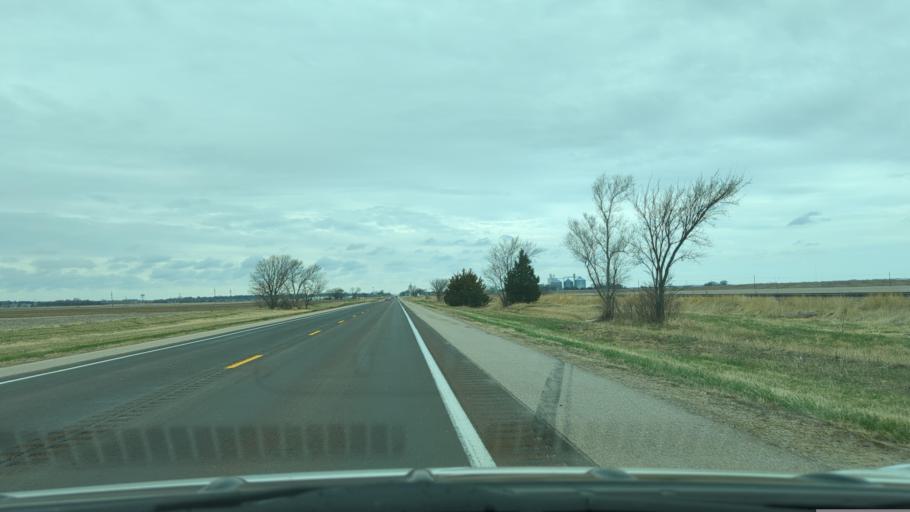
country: US
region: Nebraska
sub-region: Lancaster County
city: Waverly
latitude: 40.9341
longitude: -96.4947
